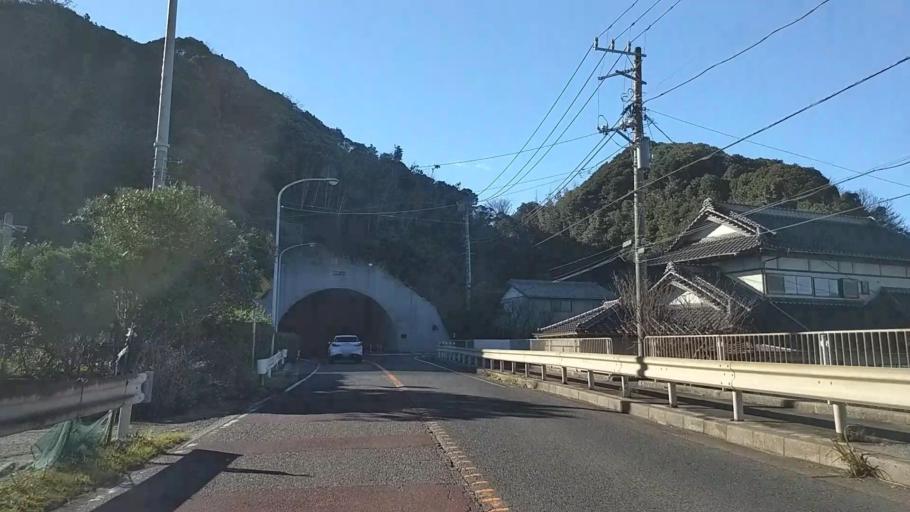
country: JP
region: Chiba
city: Futtsu
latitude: 35.1778
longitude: 139.8186
